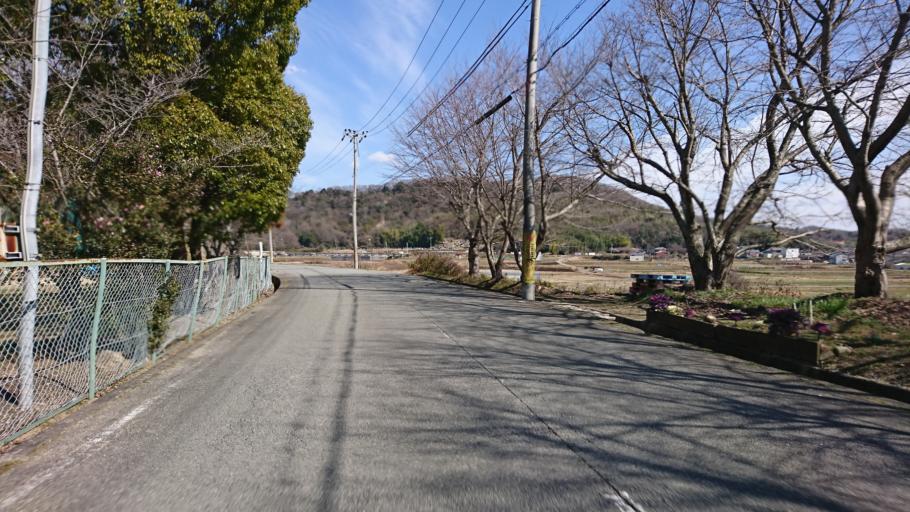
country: JP
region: Hyogo
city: Kakogawacho-honmachi
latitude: 34.8273
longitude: 134.8171
